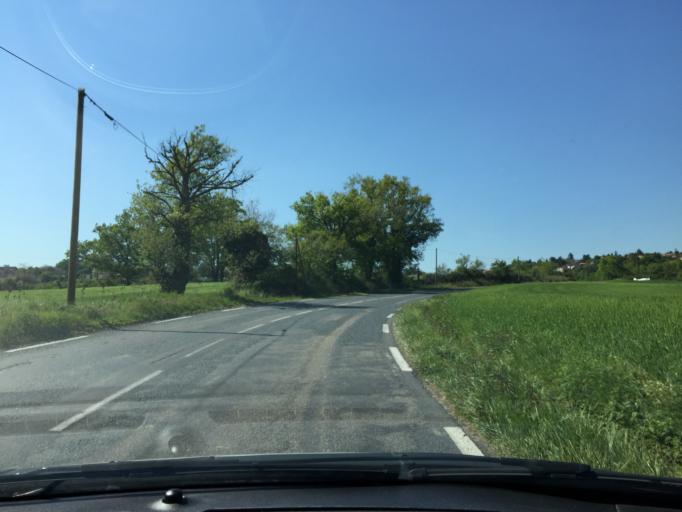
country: FR
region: Rhone-Alpes
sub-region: Departement du Rhone
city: Mornant
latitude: 45.6054
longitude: 4.6861
